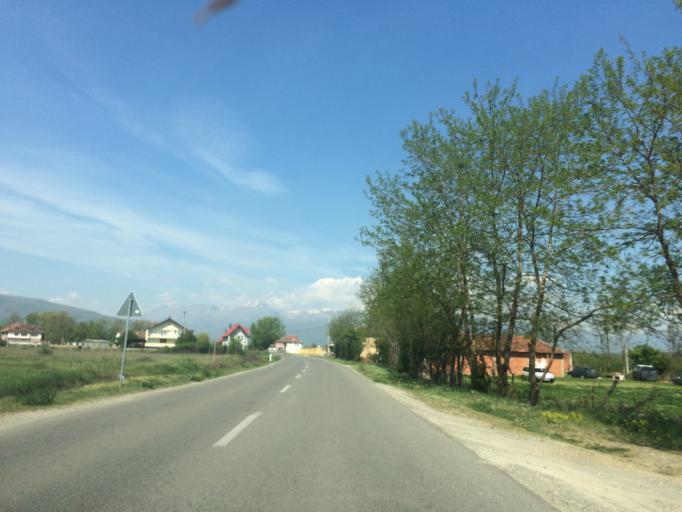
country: XK
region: Gjakova
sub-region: Komuna e Gjakoves
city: Gjakove
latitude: 42.3705
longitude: 20.3568
